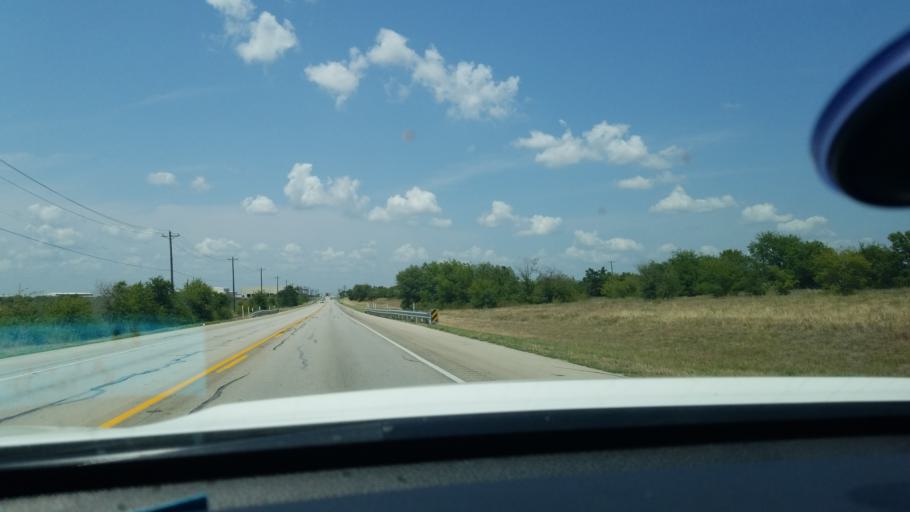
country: US
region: Texas
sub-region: Tarrant County
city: Eagle Mountain
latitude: 32.9289
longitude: -97.4144
